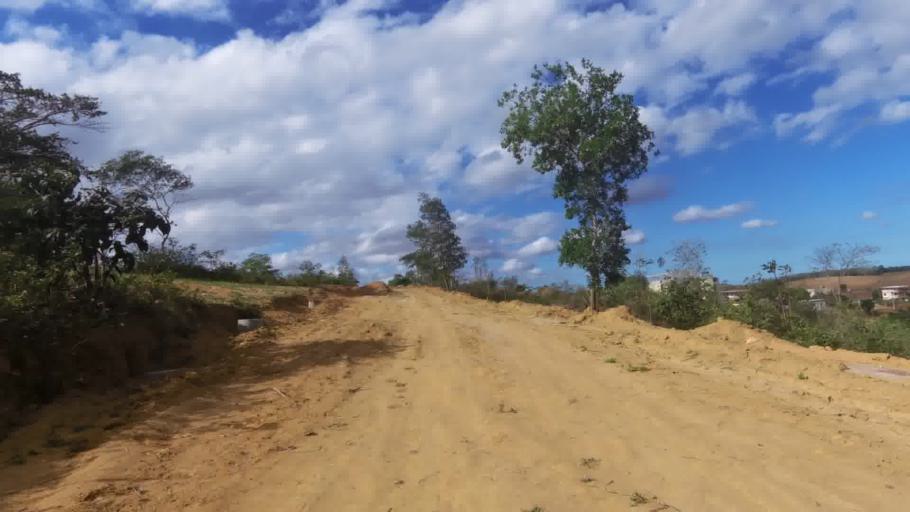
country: BR
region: Espirito Santo
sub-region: Marataizes
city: Marataizes
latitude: -21.1046
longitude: -41.0470
